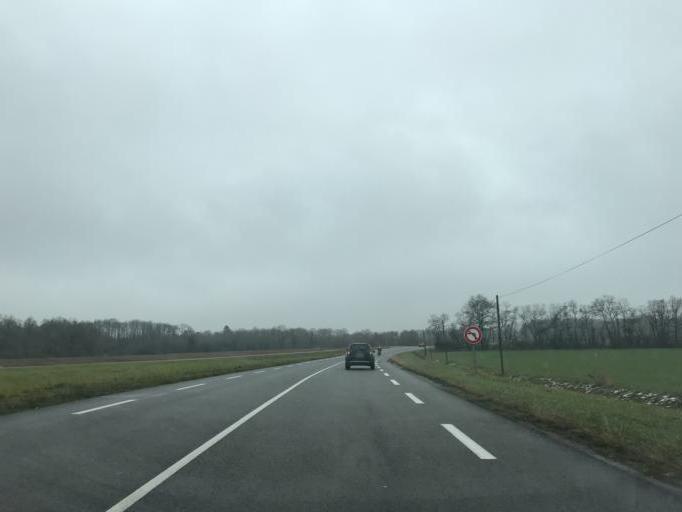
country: FR
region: Rhone-Alpes
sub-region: Departement de l'Ain
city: Villars-les-Dombes
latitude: 46.0163
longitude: 5.0525
